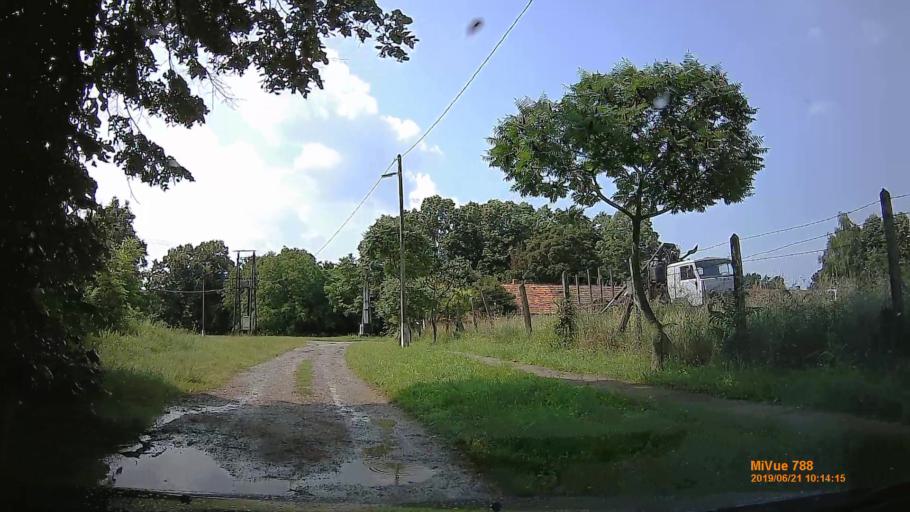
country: HU
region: Baranya
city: Buekkoesd
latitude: 46.1948
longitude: 17.9566
